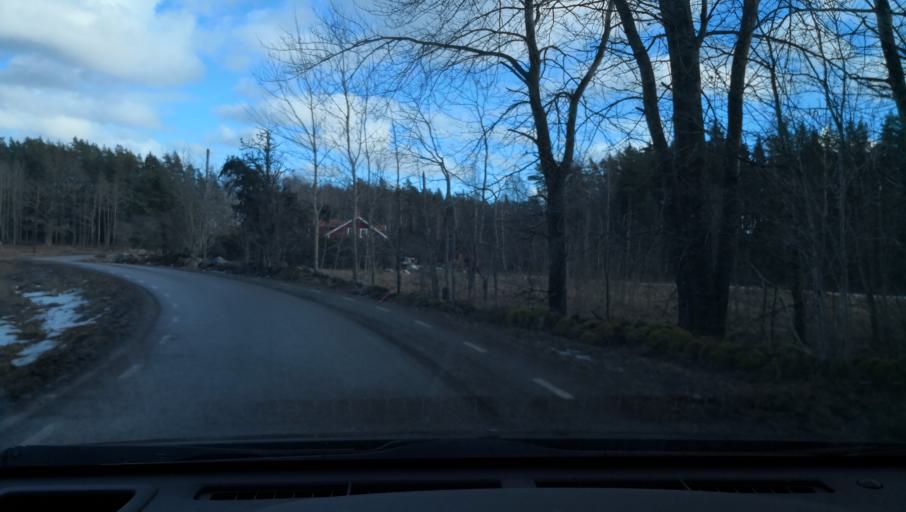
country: SE
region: Vaestmanland
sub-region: Arboga Kommun
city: Arboga
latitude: 59.3168
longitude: 15.7632
